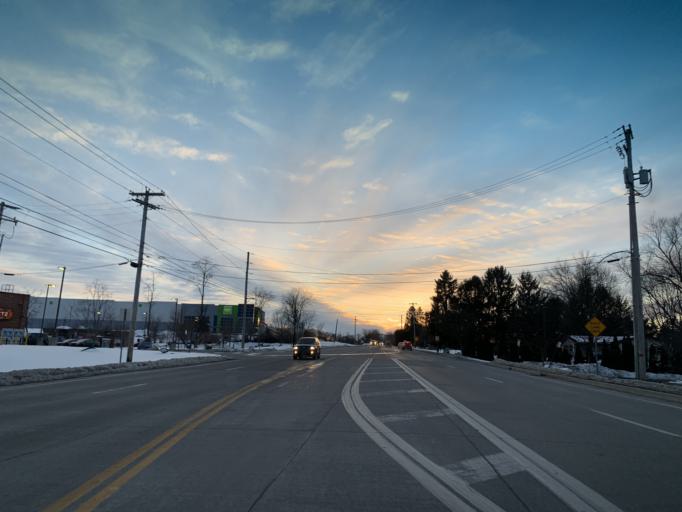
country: US
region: Pennsylvania
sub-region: Cumberland County
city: Carlisle
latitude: 40.1911
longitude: -77.2414
